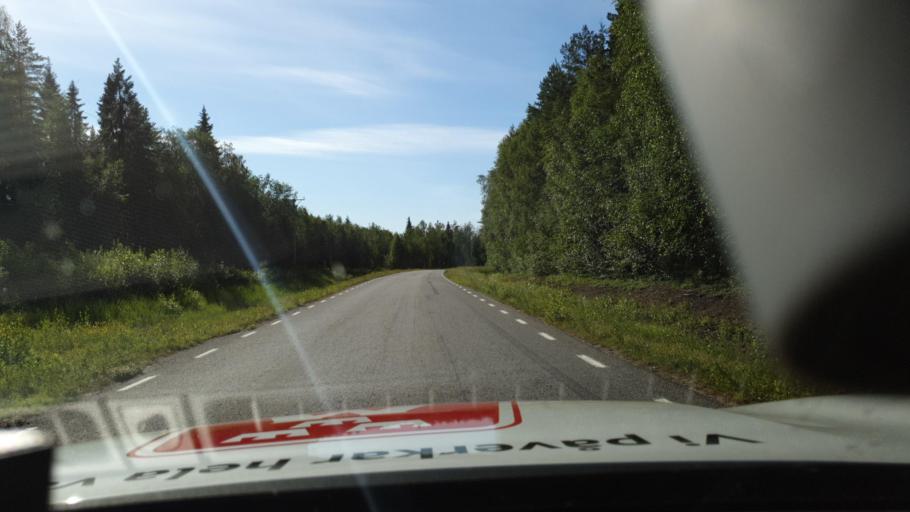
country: SE
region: Norrbotten
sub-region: Kalix Kommun
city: Toere
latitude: 65.8962
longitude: 22.6278
